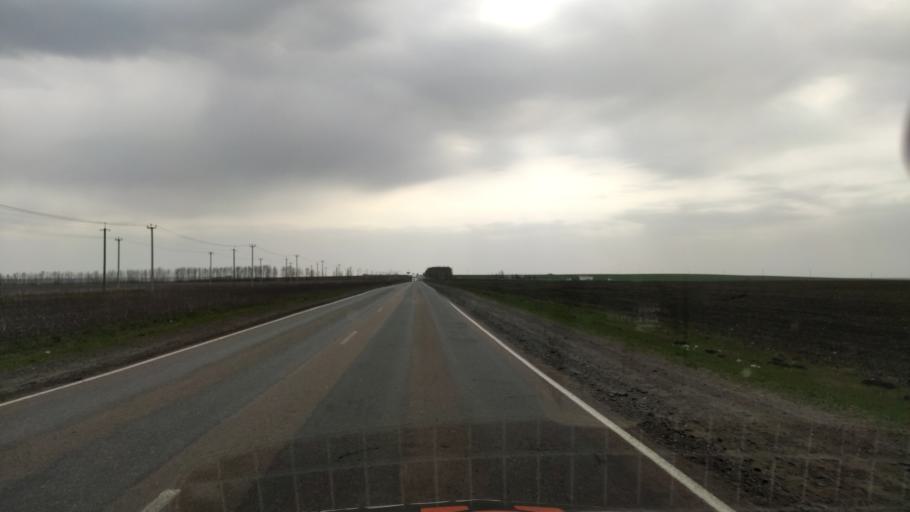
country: RU
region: Kursk
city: Gorshechnoye
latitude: 51.5133
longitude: 38.0064
